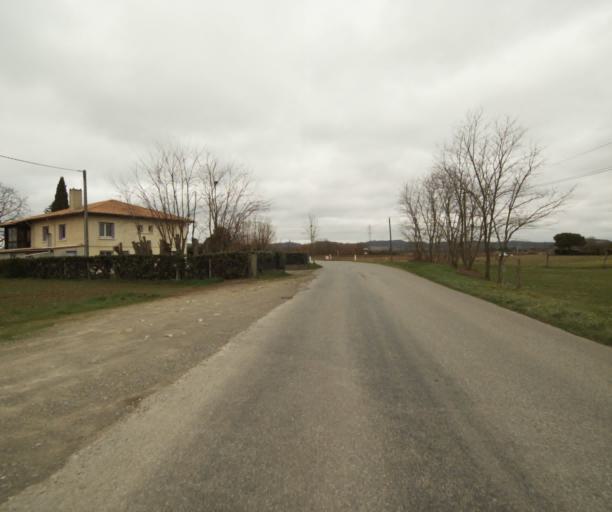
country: FR
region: Midi-Pyrenees
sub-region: Departement de l'Ariege
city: Pamiers
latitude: 43.1388
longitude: 1.6288
